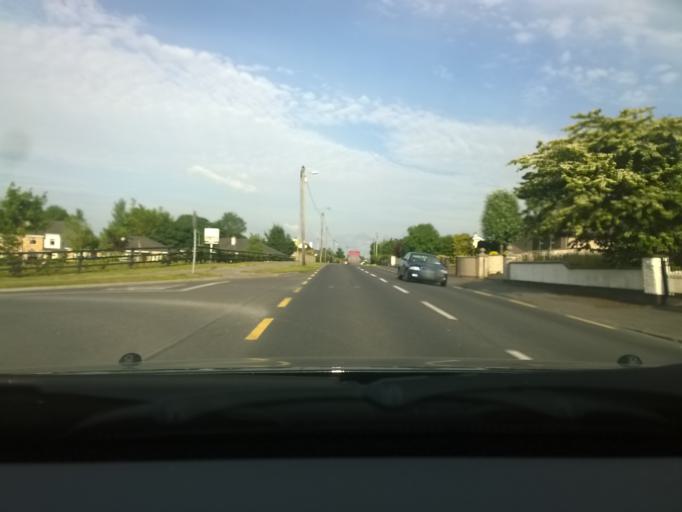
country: IE
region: Leinster
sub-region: Kildare
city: Rathangan
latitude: 53.2175
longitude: -6.9835
